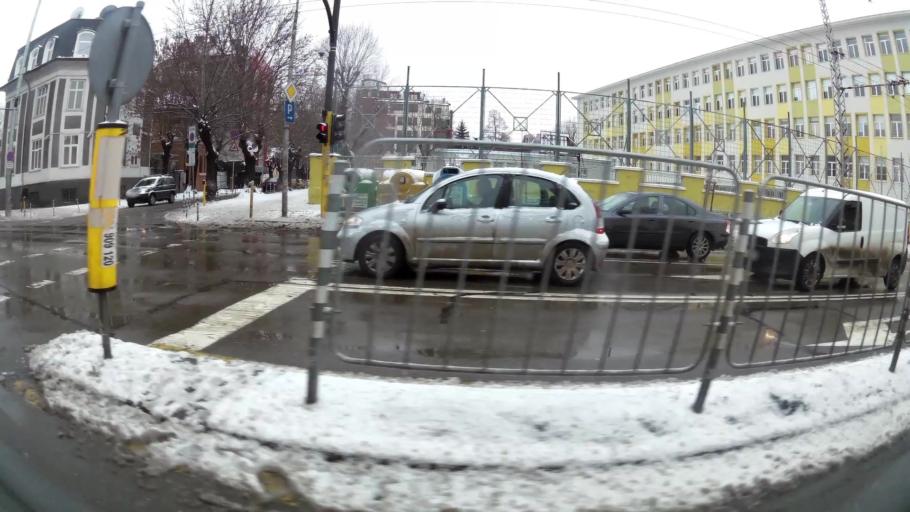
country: BG
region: Sofia-Capital
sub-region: Stolichna Obshtina
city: Sofia
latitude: 42.7016
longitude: 23.3338
